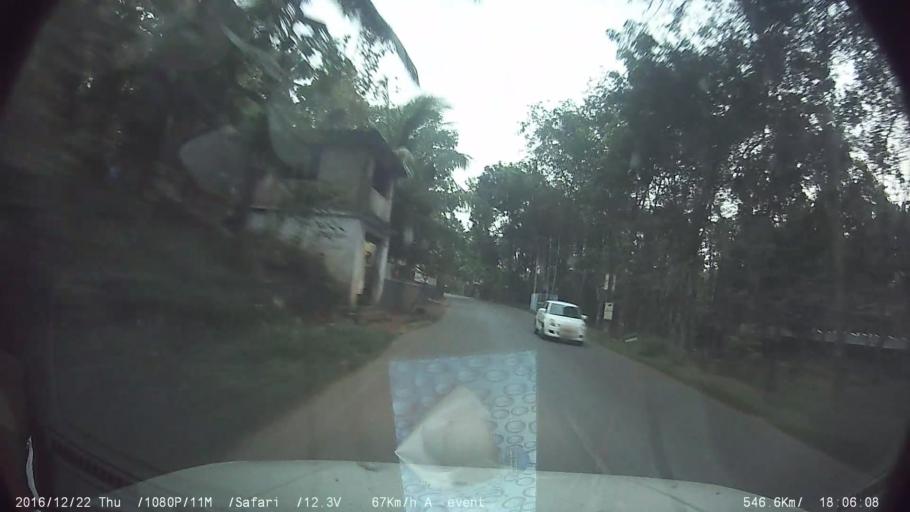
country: IN
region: Kerala
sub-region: Kottayam
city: Palackattumala
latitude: 9.8221
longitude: 76.6083
